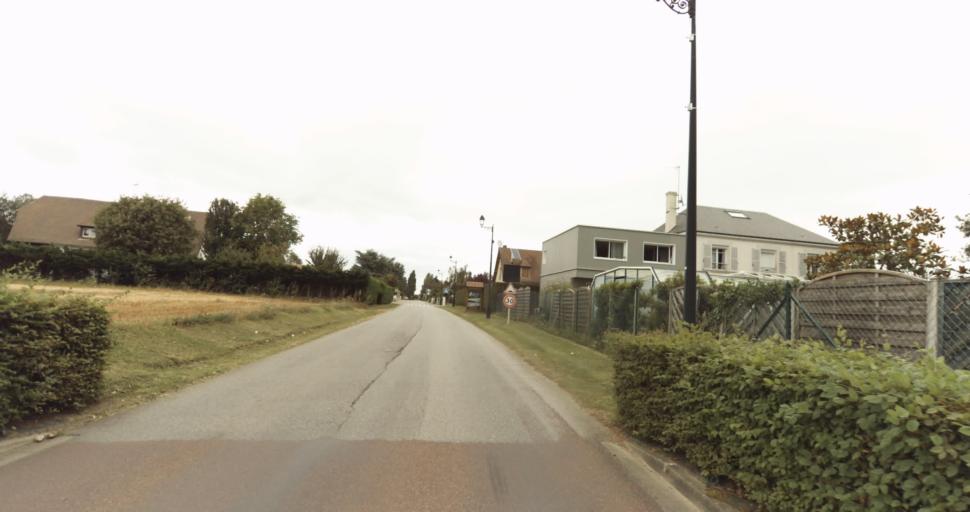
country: FR
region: Haute-Normandie
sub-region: Departement de l'Eure
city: Gravigny
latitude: 49.0345
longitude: 1.2019
